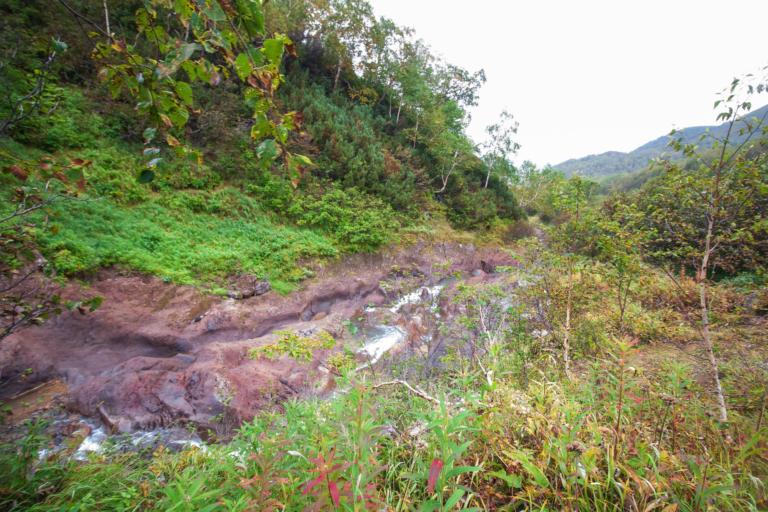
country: RU
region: Kamtsjatka
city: Petropavlovsk-Kamchatsky
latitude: 53.5872
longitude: 158.9133
